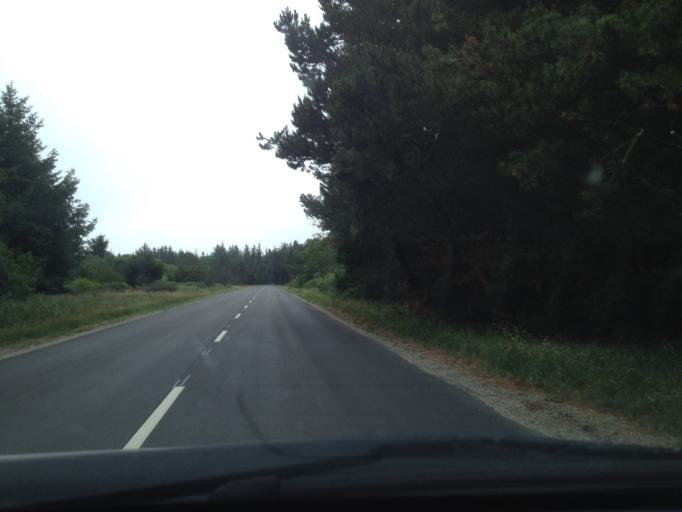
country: DK
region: South Denmark
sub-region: Varde Kommune
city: Oksbol
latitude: 55.5603
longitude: 8.1679
